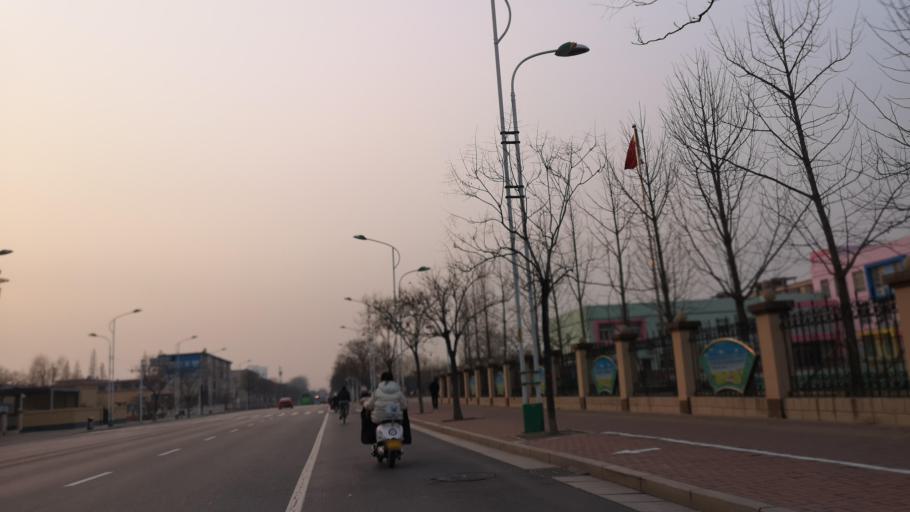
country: CN
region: Henan Sheng
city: Zhongyuanlu
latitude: 35.7841
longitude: 115.0783
